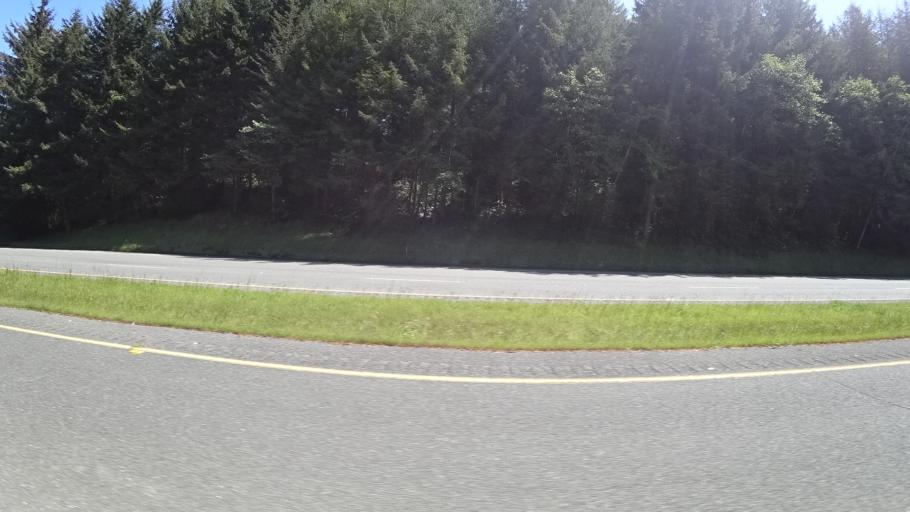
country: US
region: California
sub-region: Humboldt County
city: Westhaven-Moonstone
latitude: 41.1014
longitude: -124.1543
